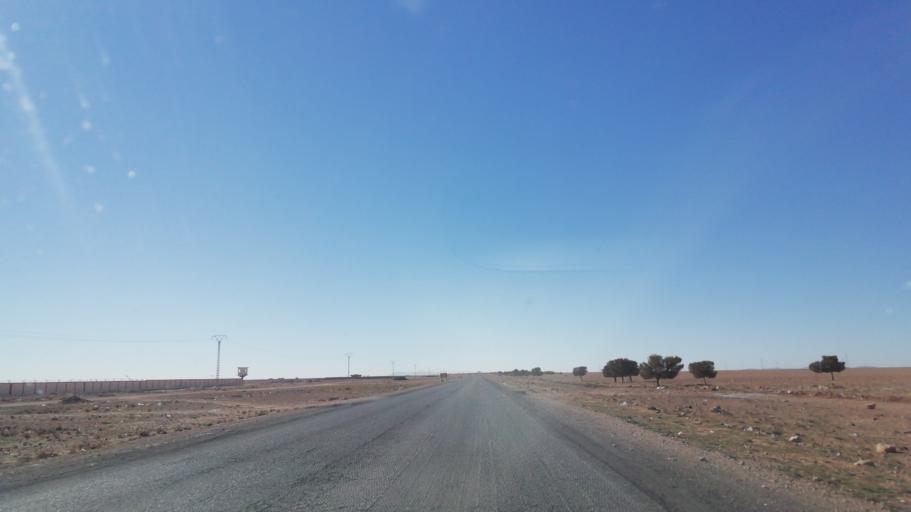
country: DZ
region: Saida
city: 'Ain el Hadjar
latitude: 34.0204
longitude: 0.0637
